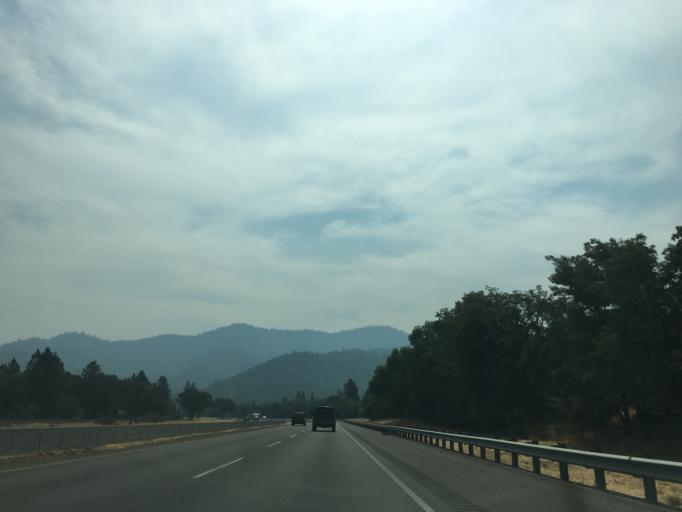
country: US
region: Oregon
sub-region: Jackson County
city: Rogue River
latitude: 42.4096
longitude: -123.1439
